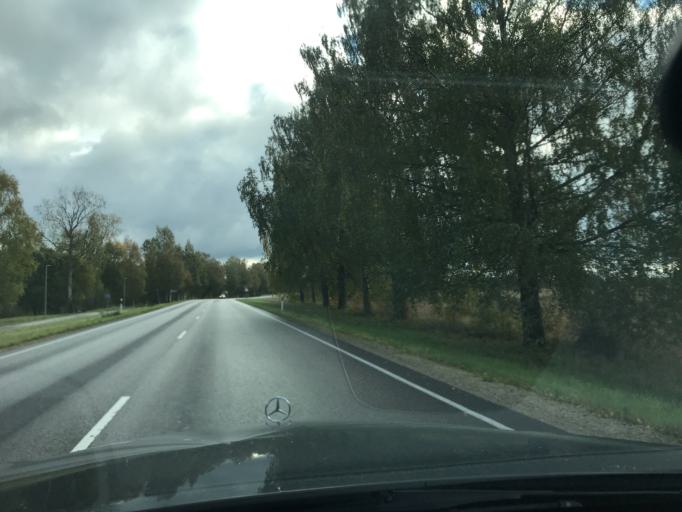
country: EE
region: Valgamaa
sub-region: Torva linn
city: Torva
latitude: 58.0297
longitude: 25.8534
